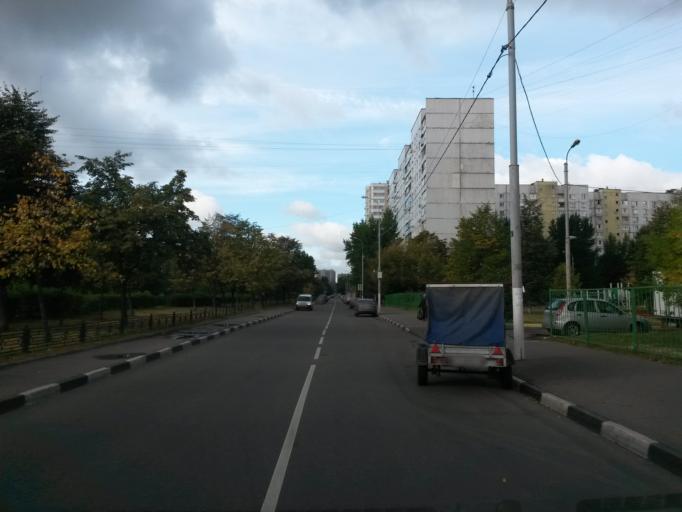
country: RU
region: Moscow
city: Mar'ino
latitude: 55.6524
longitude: 37.7190
